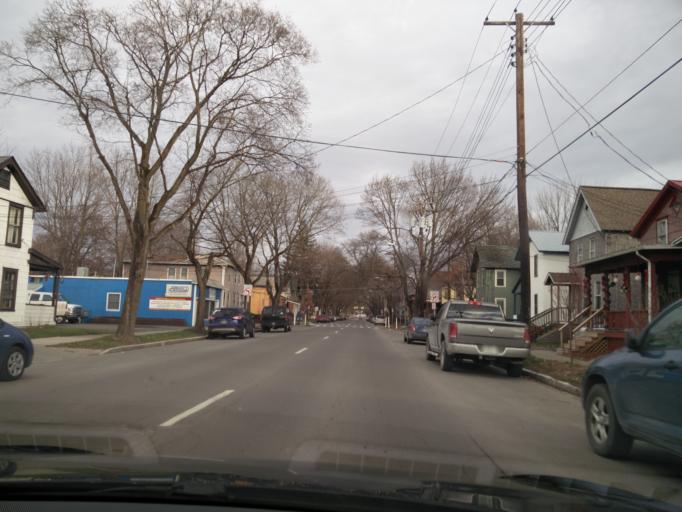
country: US
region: New York
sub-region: Tompkins County
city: Ithaca
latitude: 42.4384
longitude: -76.5071
